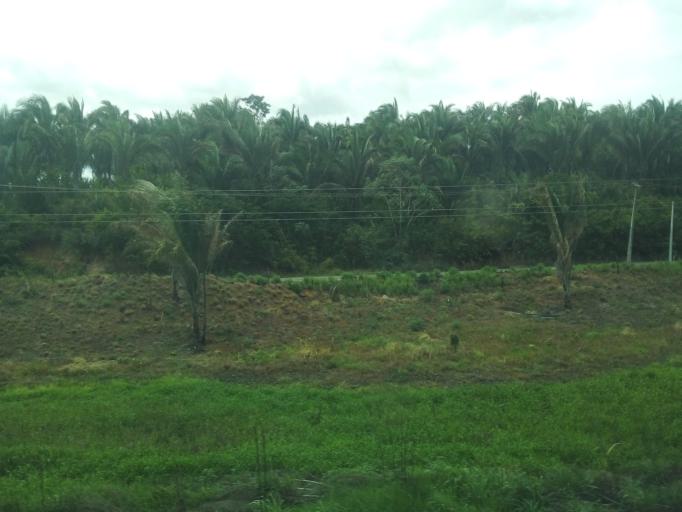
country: BR
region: Maranhao
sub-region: Santa Ines
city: Santa Ines
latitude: -3.6883
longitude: -45.9086
